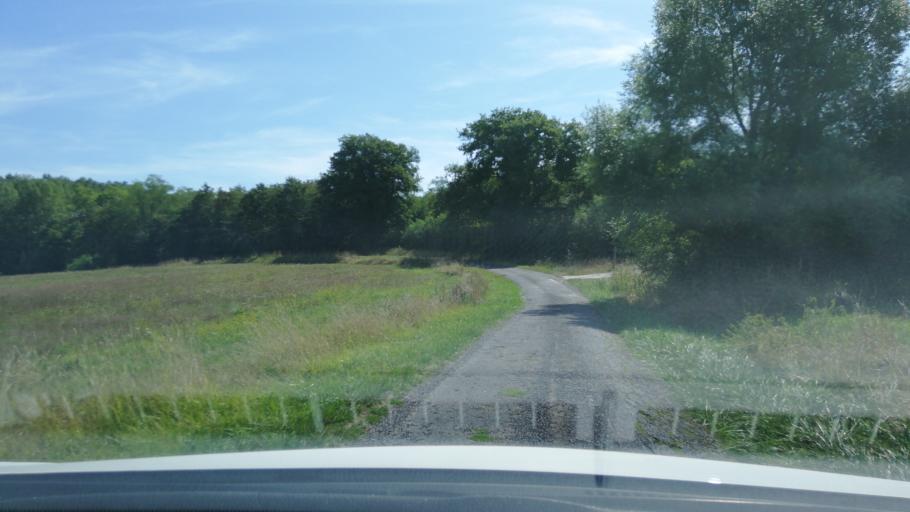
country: FR
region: Centre
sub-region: Departement d'Indre-et-Loire
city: Mazieres-de-Touraine
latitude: 47.3912
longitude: 0.4394
